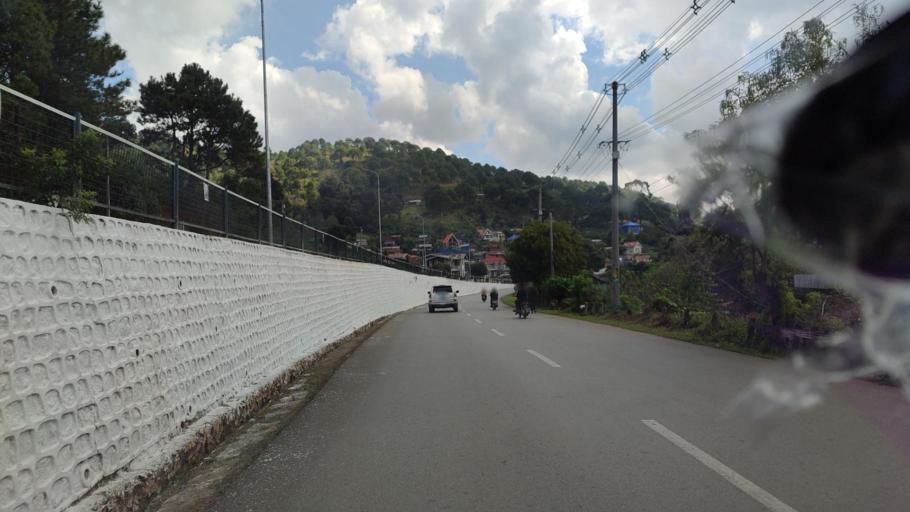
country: MM
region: Mandalay
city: Yamethin
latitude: 20.6357
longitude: 96.5720
